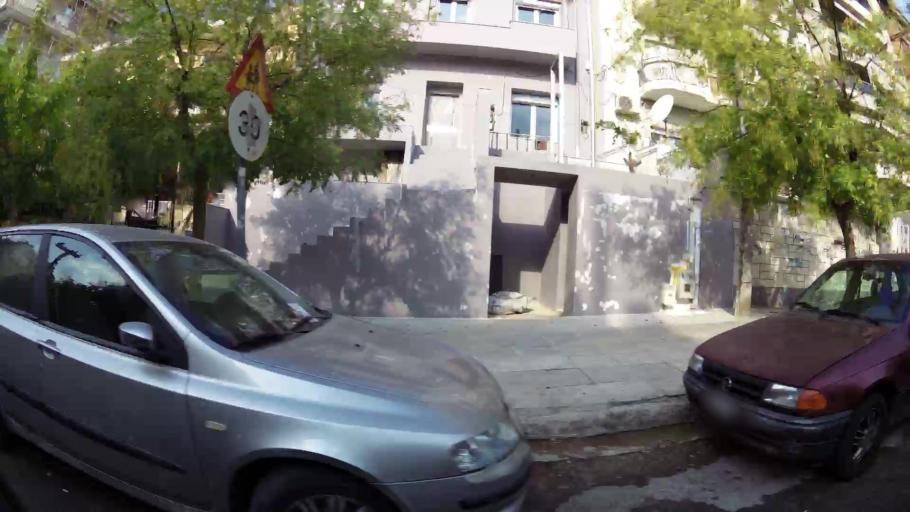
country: GR
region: Attica
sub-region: Nomarchia Athinas
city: Kipseli
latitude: 38.0072
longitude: 23.7452
